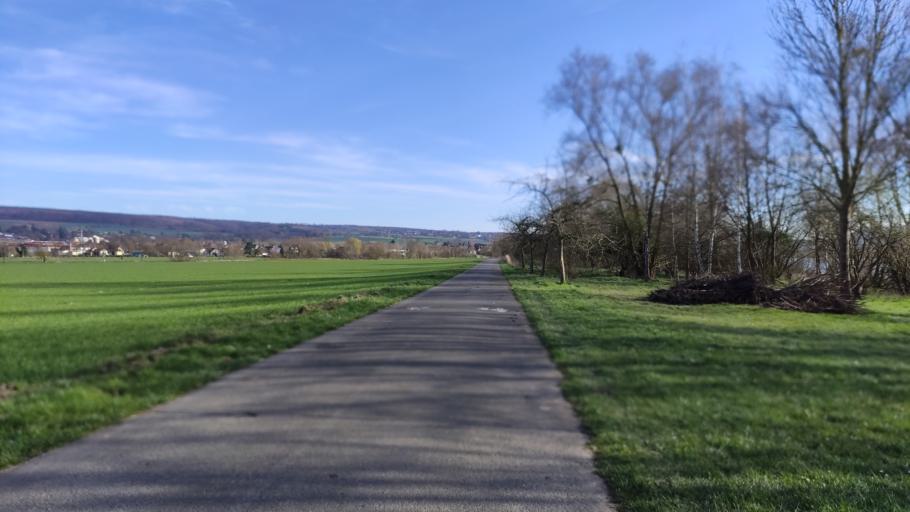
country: DE
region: Lower Saxony
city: Boffzen
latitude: 51.7593
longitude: 9.3814
